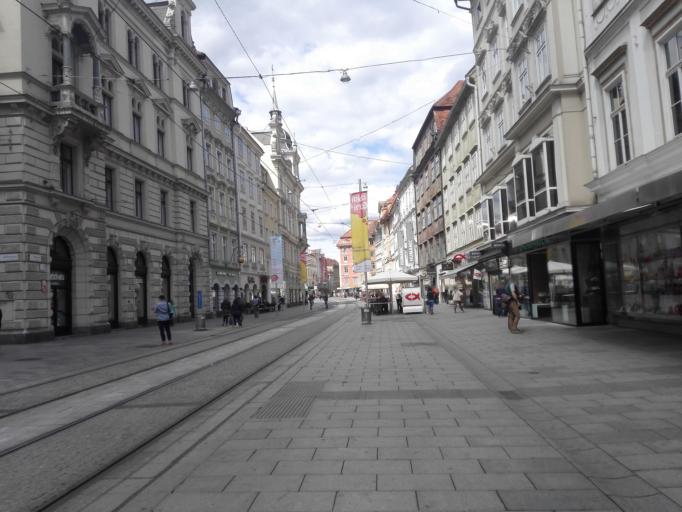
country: AT
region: Styria
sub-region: Graz Stadt
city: Graz
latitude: 47.0703
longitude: 15.4396
